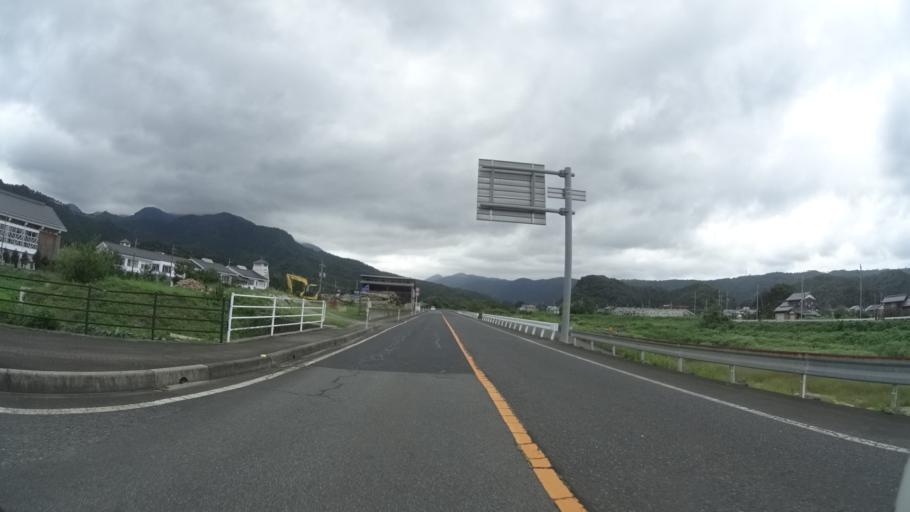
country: JP
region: Tottori
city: Tottori
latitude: 35.4620
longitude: 134.0559
